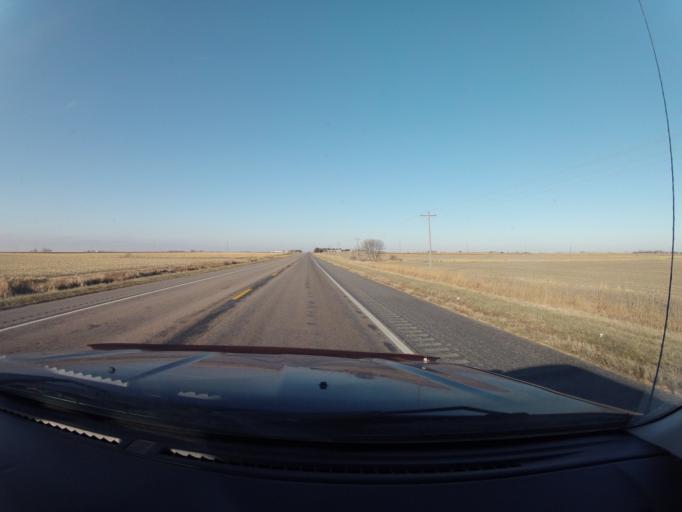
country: US
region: Nebraska
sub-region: Kearney County
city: Minden
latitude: 40.5308
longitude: -98.9519
